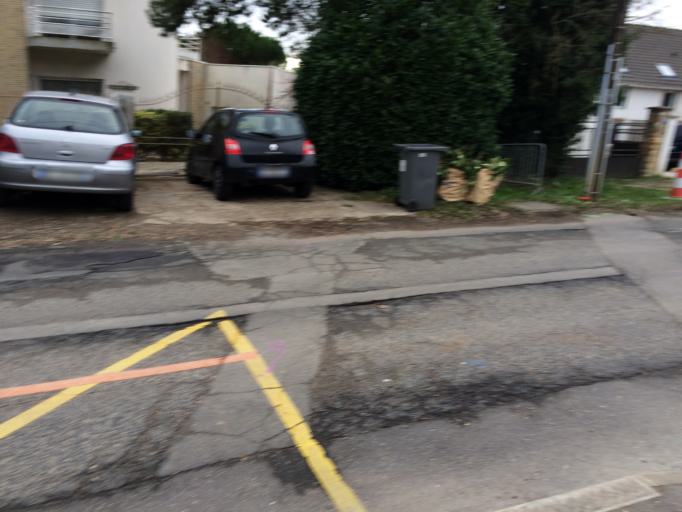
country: FR
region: Ile-de-France
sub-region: Departement de l'Essonne
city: Villebon-sur-Yvette
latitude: 48.7095
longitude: 2.2253
